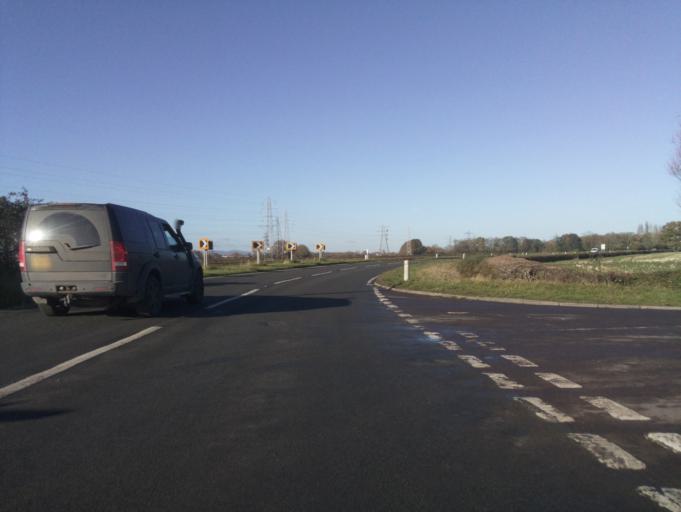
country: GB
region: England
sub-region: Somerset
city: Westonzoyland
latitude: 51.1128
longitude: -2.9603
